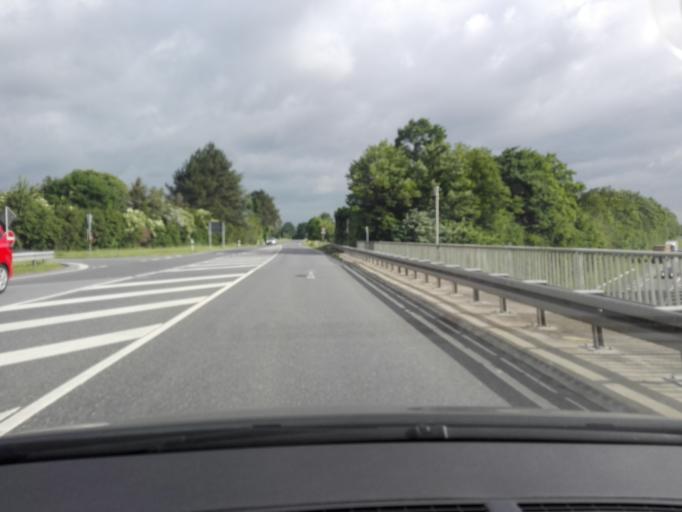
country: DE
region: North Rhine-Westphalia
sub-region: Regierungsbezirk Arnsberg
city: Unna
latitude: 51.5074
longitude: 7.7015
